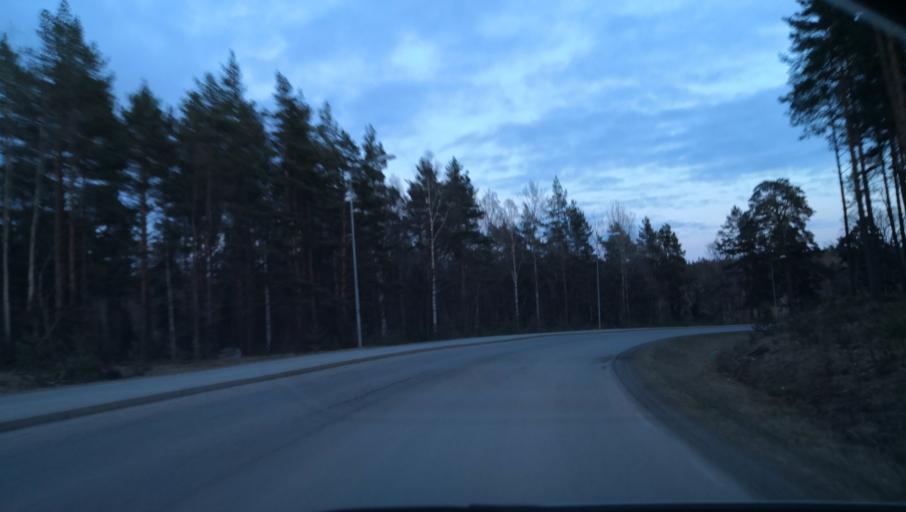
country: SE
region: Stockholm
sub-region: Nacka Kommun
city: Boo
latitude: 59.3410
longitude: 18.2971
